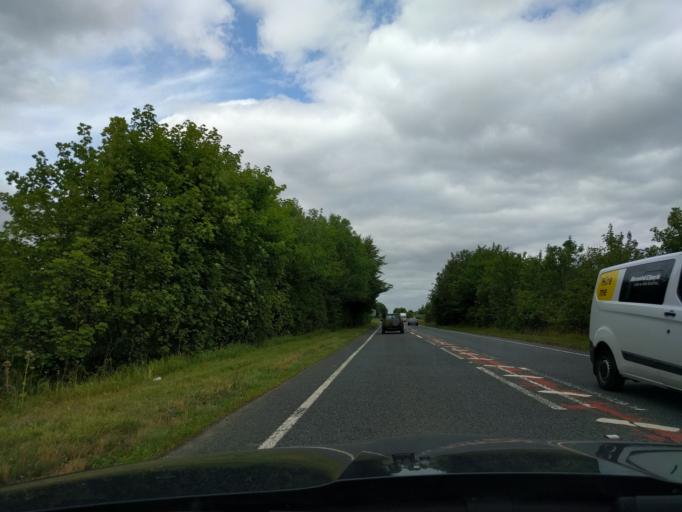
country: GB
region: England
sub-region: Northumberland
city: Belford
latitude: 55.5569
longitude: -1.7896
